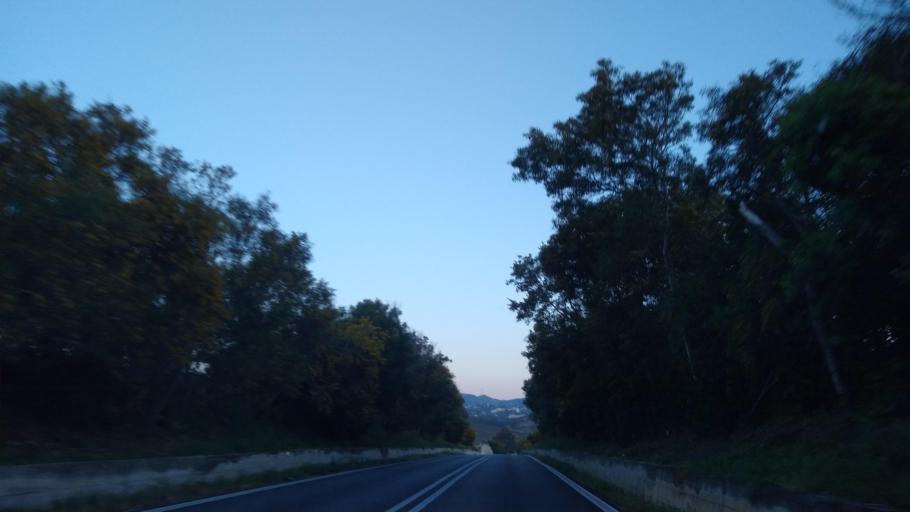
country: IT
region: Sicily
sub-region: Trapani
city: Alcamo
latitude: 38.0126
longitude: 12.9605
